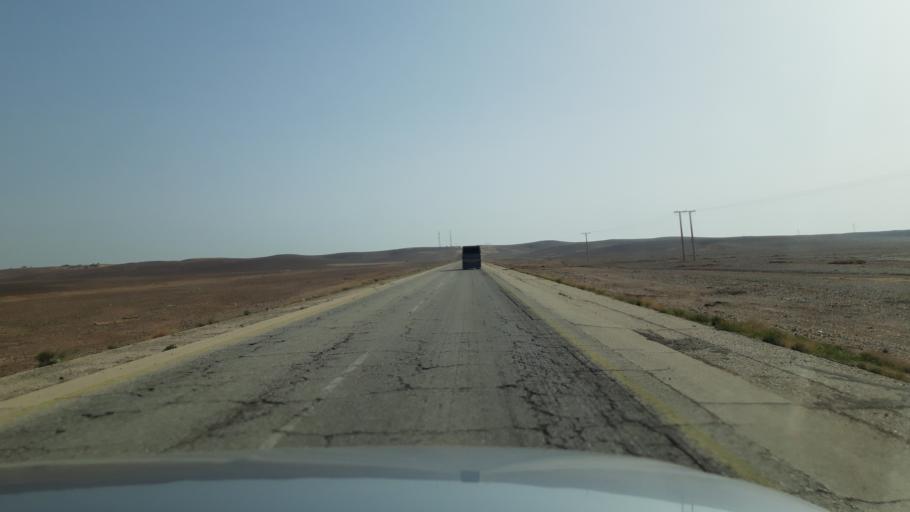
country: JO
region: Amman
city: Al Azraq ash Shamali
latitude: 31.8469
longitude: 36.6598
